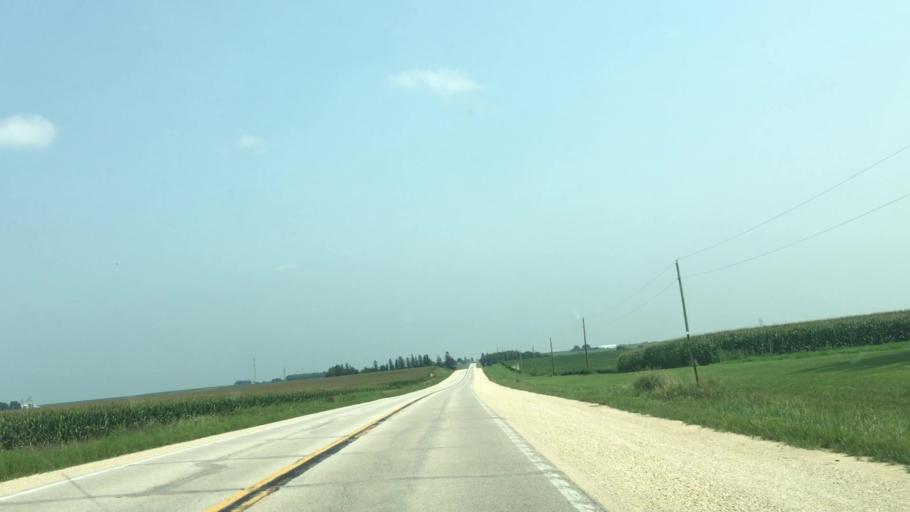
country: US
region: Iowa
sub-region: Fayette County
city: Oelwein
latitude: 42.6798
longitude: -91.8630
